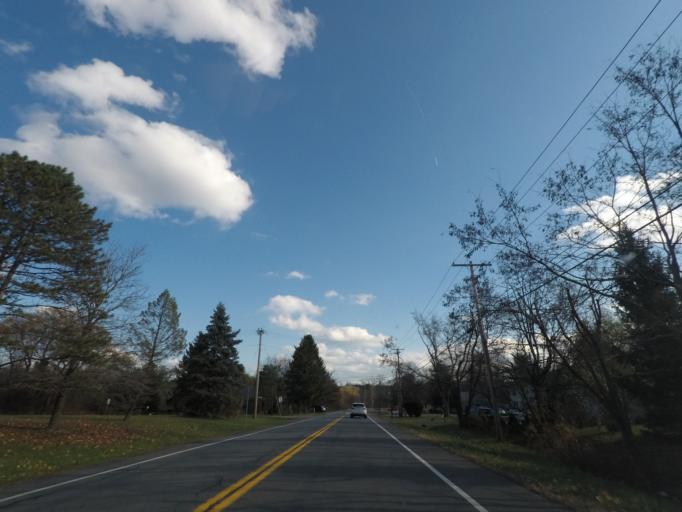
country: US
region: New York
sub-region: Schenectady County
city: Niskayuna
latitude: 42.8043
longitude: -73.8636
